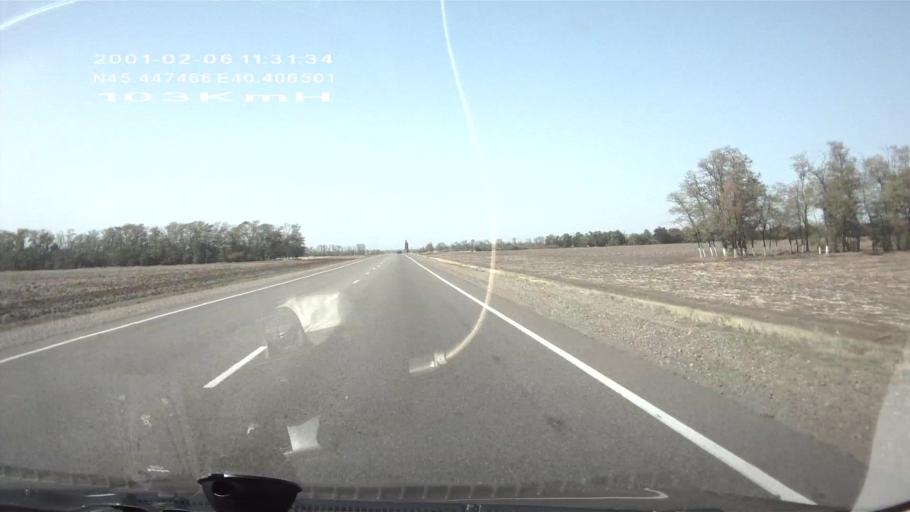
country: RU
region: Krasnodarskiy
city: Kazanskaya
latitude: 45.4483
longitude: 40.4045
